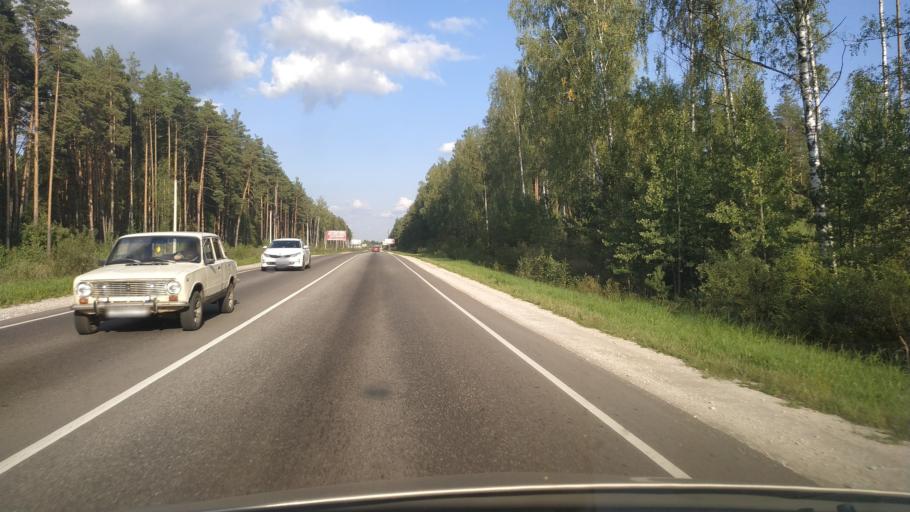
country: RU
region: Moskovskaya
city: Shaturtorf
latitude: 55.5787
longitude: 39.4476
